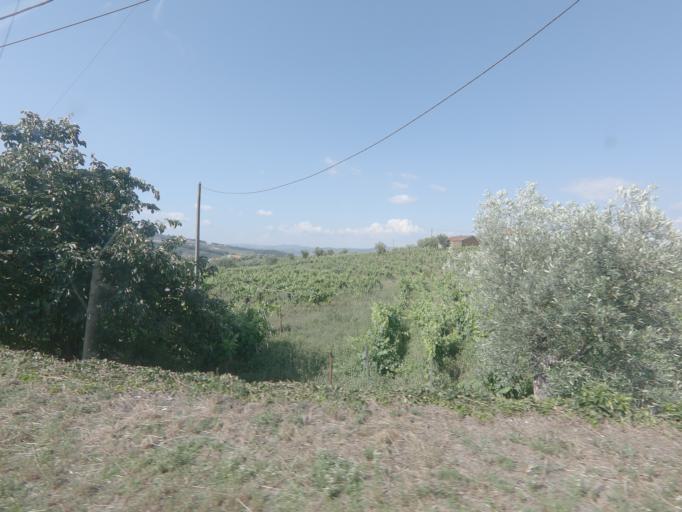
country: PT
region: Vila Real
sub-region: Sabrosa
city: Sabrosa
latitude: 41.2440
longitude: -7.5716
